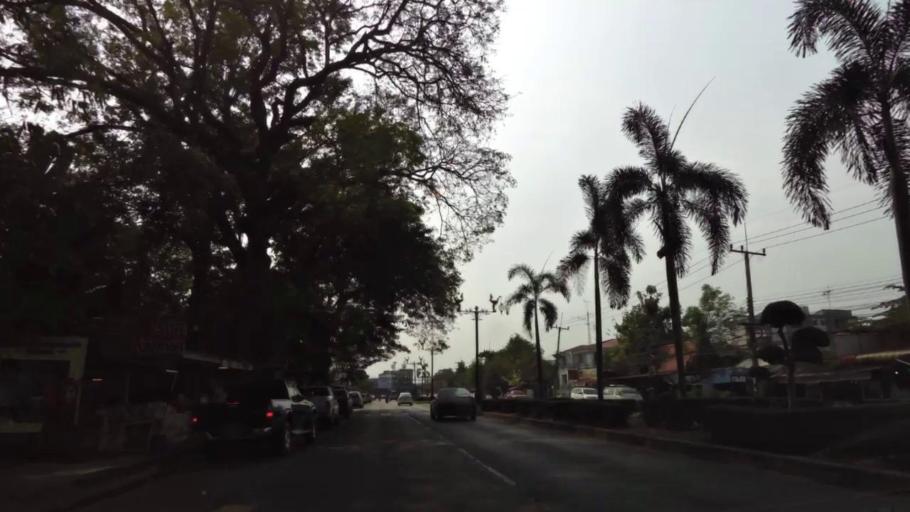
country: TH
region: Phra Nakhon Si Ayutthaya
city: Phra Nakhon Si Ayutthaya
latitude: 14.3473
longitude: 100.5651
